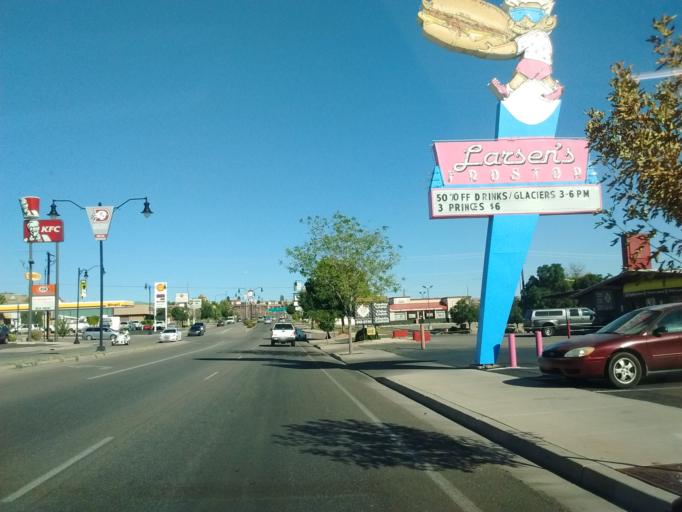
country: US
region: Utah
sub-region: Washington County
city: Saint George
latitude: 37.1097
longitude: -113.5652
